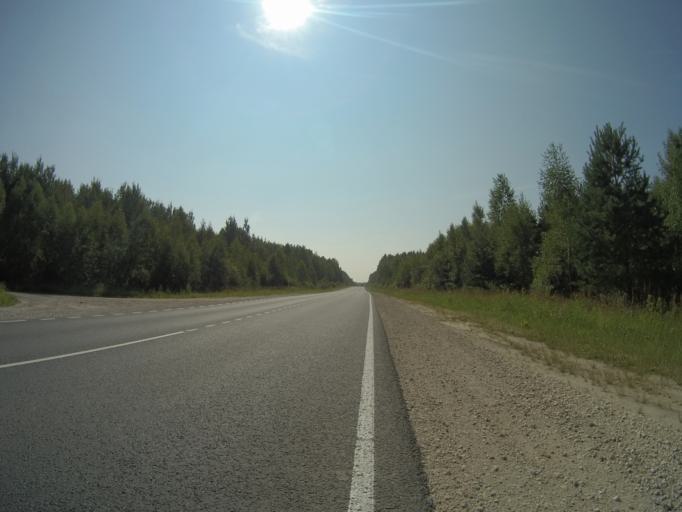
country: RU
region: Vladimir
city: Anopino
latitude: 55.8322
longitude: 40.6456
